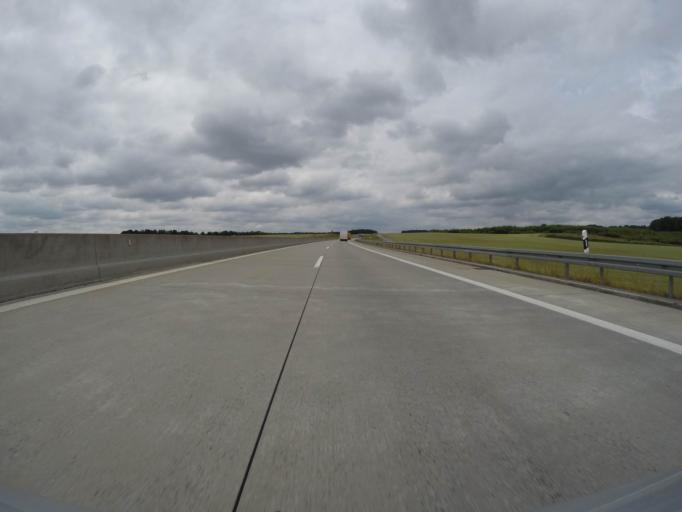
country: DE
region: Bavaria
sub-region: Regierungsbezirk Unterfranken
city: Strahlungen
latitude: 50.2731
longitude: 10.2495
